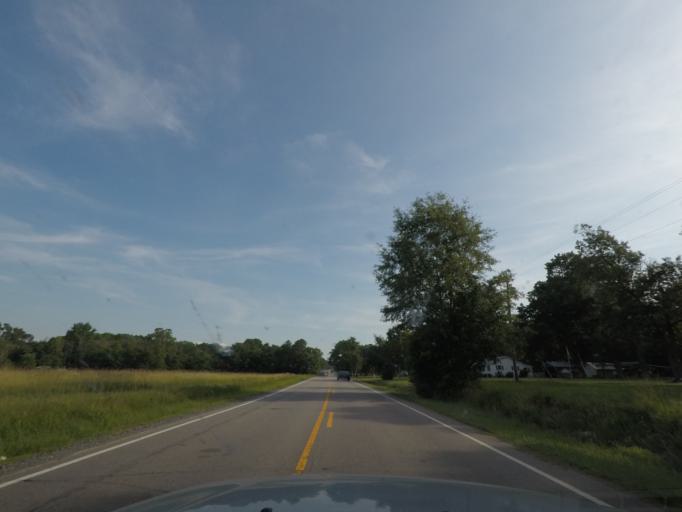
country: US
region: Virginia
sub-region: Mecklenburg County
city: Clarksville
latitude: 36.4978
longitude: -78.5423
